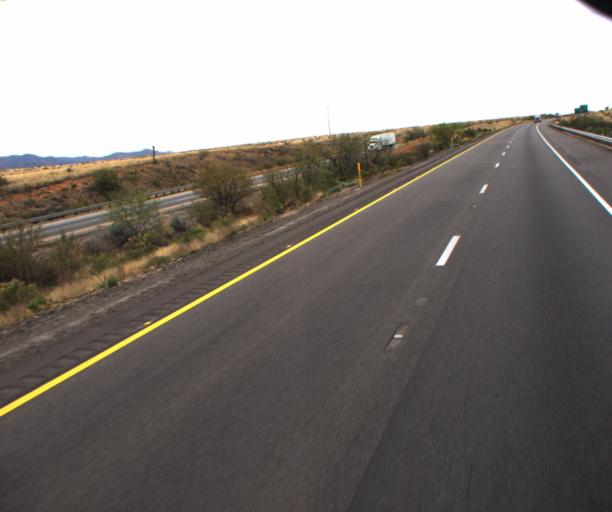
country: US
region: Arizona
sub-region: Cochise County
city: Willcox
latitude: 32.0949
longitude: -110.0353
